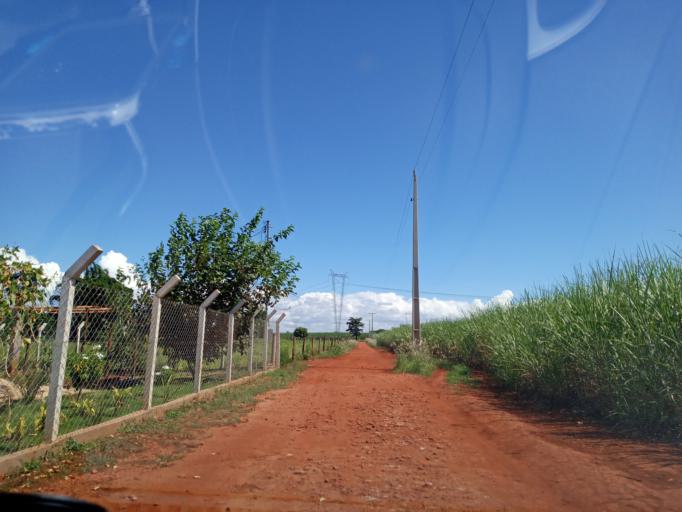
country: BR
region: Goias
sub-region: Itumbiara
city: Itumbiara
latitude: -18.4338
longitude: -49.1178
